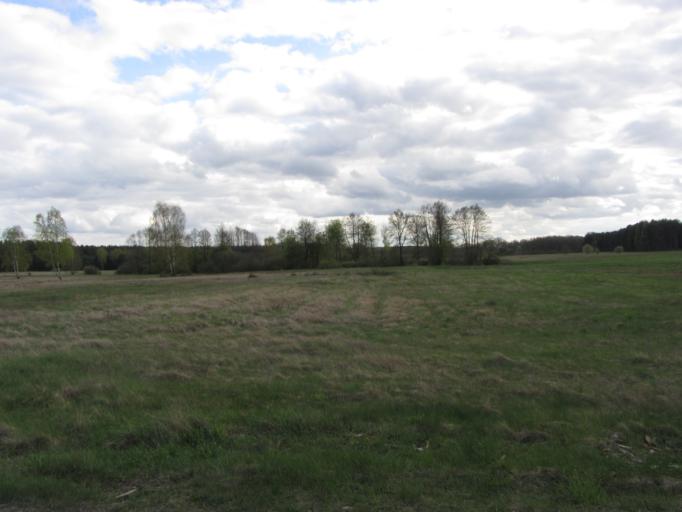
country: PL
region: Lubusz
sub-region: Powiat wschowski
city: Slawa
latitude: 51.8721
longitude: 16.0023
